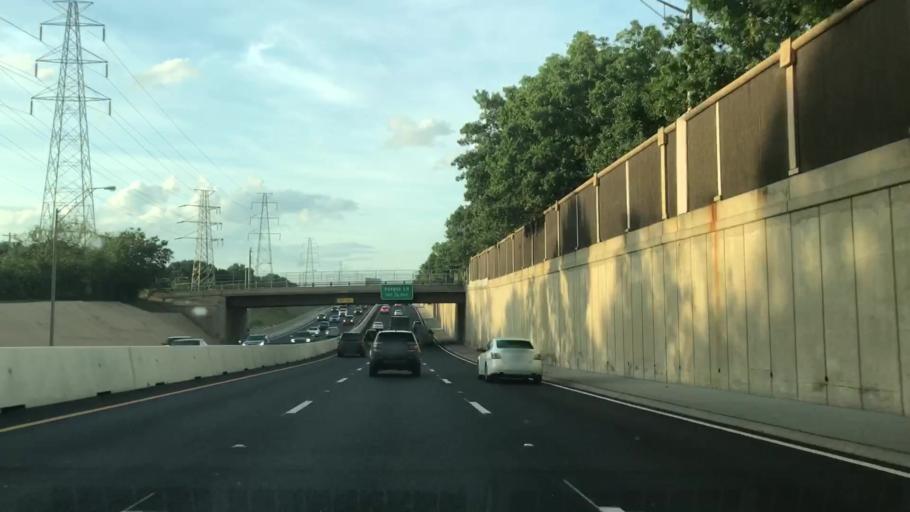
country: US
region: Texas
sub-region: Dallas County
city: University Park
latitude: 32.9015
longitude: -96.8117
